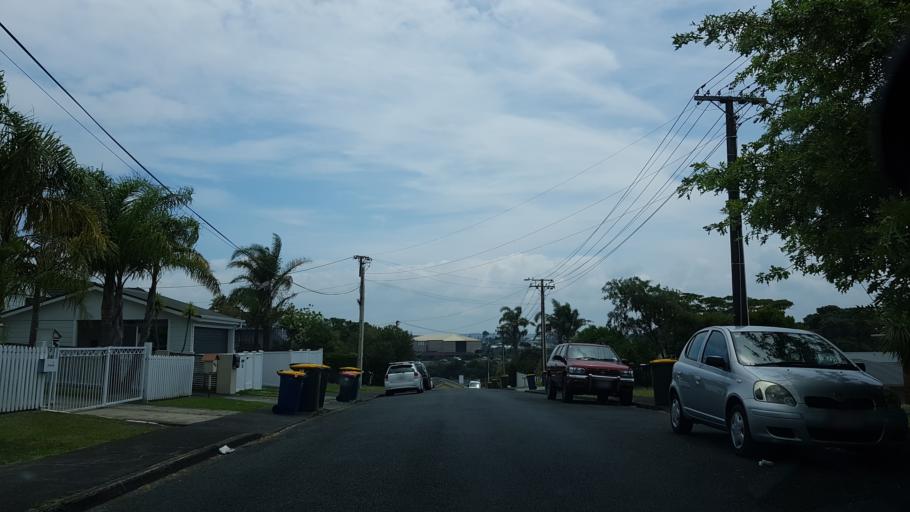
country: NZ
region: Auckland
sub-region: Auckland
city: North Shore
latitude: -36.7983
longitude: 174.7724
